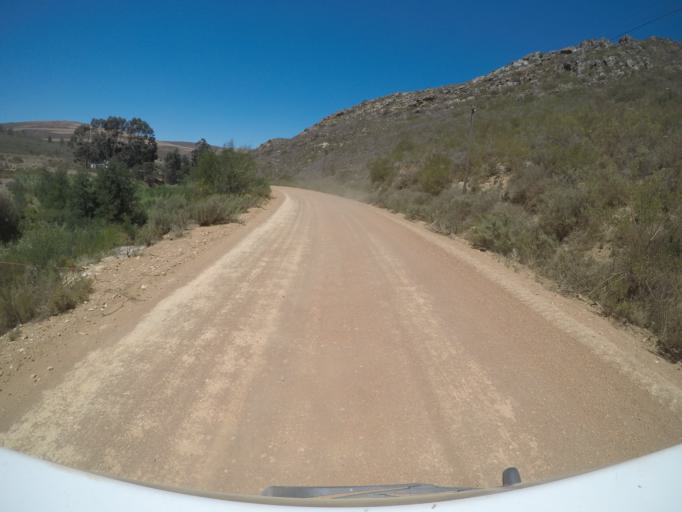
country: ZA
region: Western Cape
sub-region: Overberg District Municipality
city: Caledon
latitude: -34.1208
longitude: 19.2356
